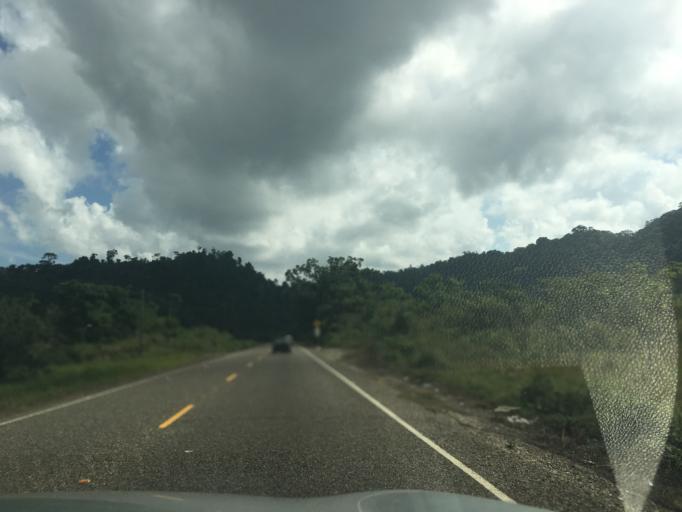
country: BZ
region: Cayo
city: Belmopan
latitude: 17.1470
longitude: -88.7001
